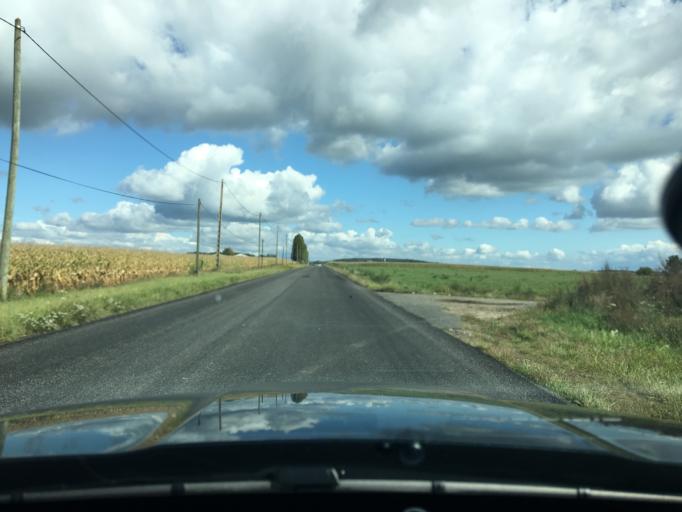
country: FR
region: Ile-de-France
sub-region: Departement du Val-d'Oise
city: Survilliers
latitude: 49.0807
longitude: 2.5356
